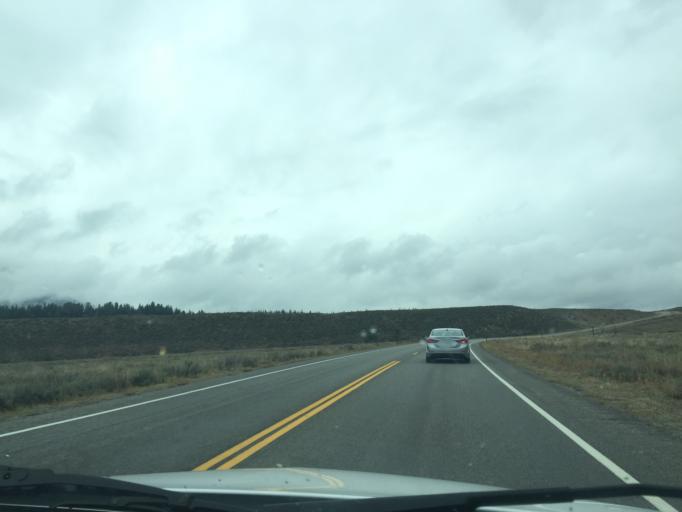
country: US
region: Wyoming
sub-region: Teton County
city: Moose Wilson Road
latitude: 43.6618
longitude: -110.7223
